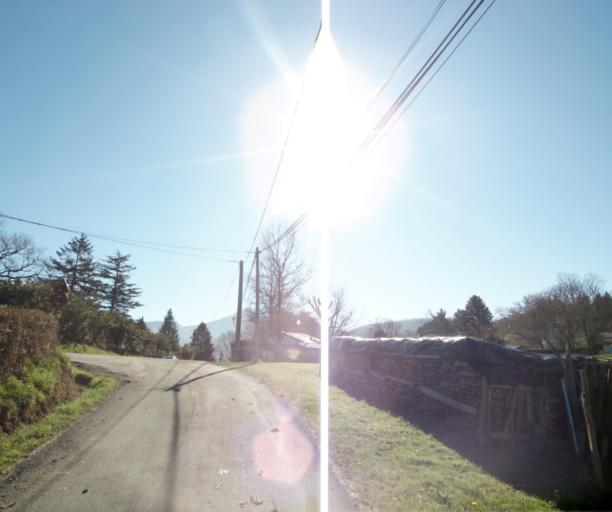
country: FR
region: Aquitaine
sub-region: Departement des Pyrenees-Atlantiques
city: Urrugne
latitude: 43.3376
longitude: -1.6870
